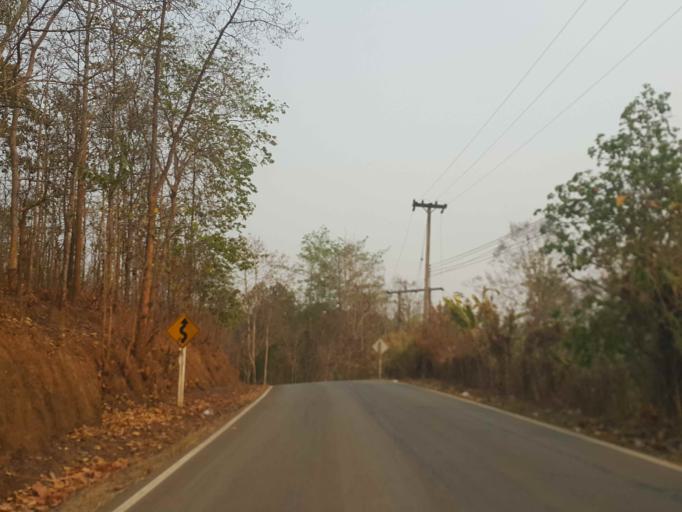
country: TH
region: Chiang Mai
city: Mae Taeng
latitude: 19.1096
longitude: 98.8980
